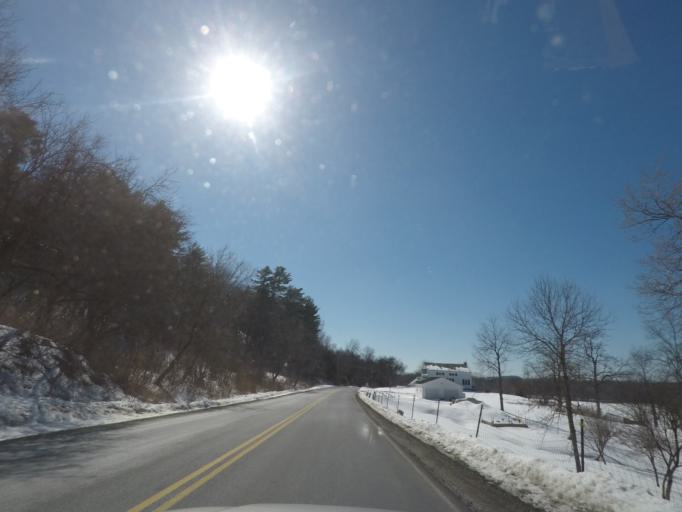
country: US
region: New York
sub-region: Saratoga County
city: Schuylerville
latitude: 43.0950
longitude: -73.5681
